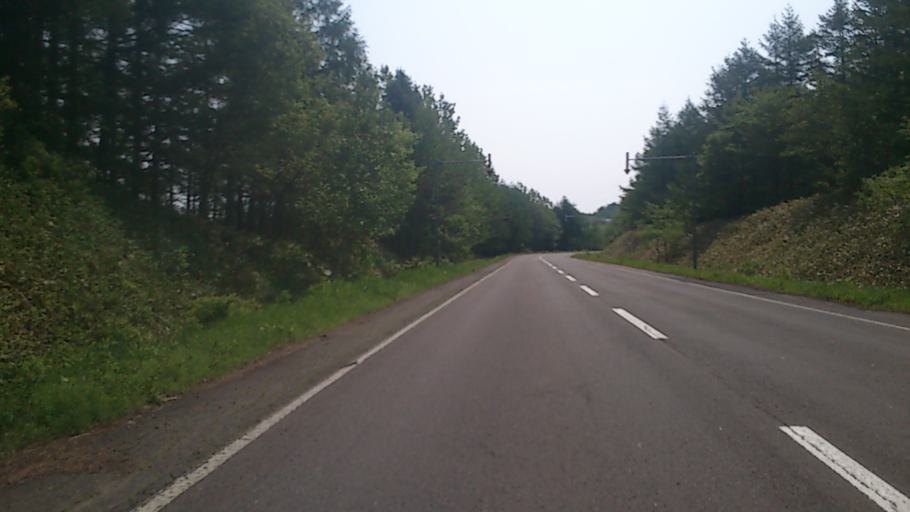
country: JP
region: Hokkaido
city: Kushiro
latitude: 43.4840
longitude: 144.5320
